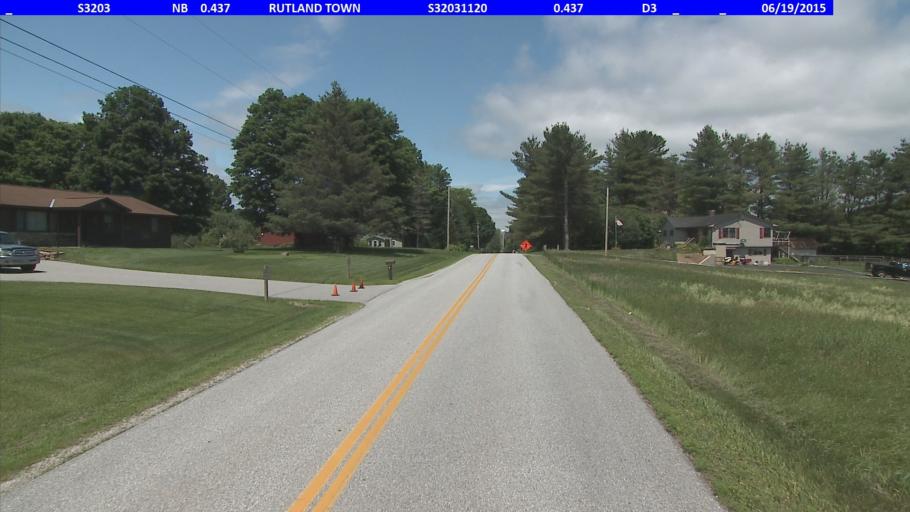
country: US
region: Vermont
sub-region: Rutland County
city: Rutland
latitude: 43.6596
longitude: -72.9983
